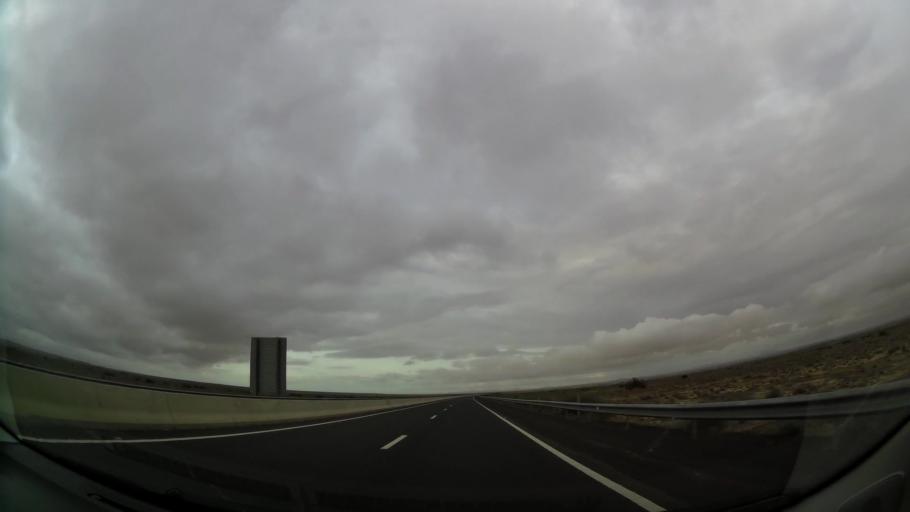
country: MA
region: Taza-Al Hoceima-Taounate
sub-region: Taza
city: Guercif
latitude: 34.3737
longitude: -3.2626
